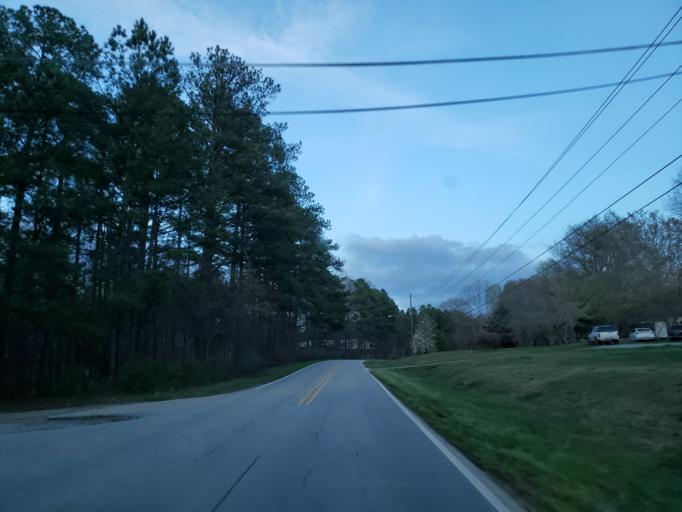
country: US
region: Georgia
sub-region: Polk County
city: Rockmart
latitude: 33.9904
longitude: -84.9594
